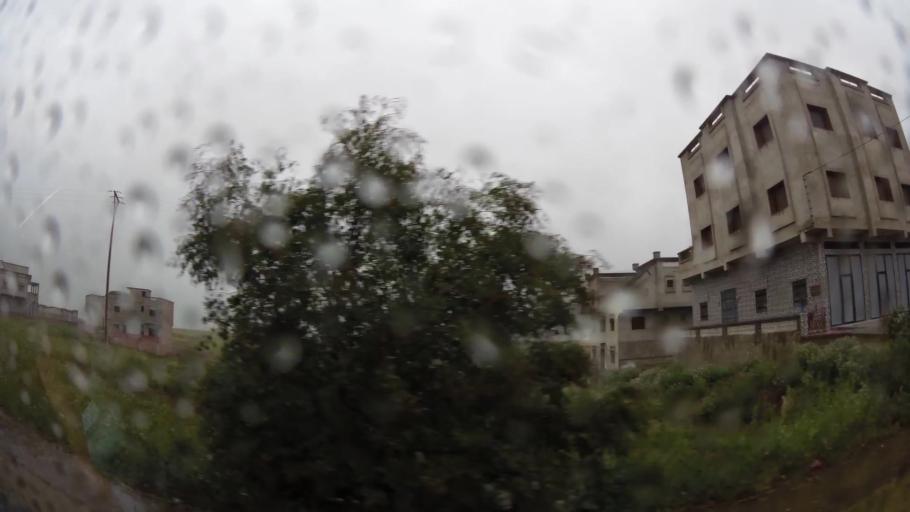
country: MA
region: Oriental
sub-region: Nador
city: Boudinar
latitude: 35.1215
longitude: -3.6452
